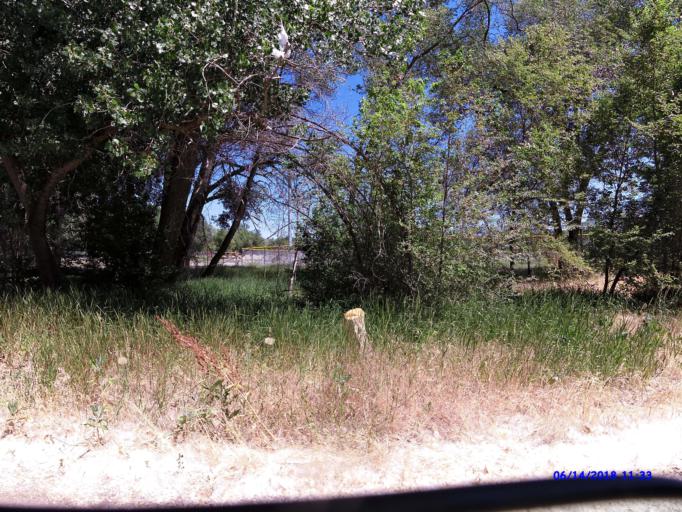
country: US
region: Utah
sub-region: Weber County
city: Ogden
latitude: 41.2192
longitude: -111.9888
